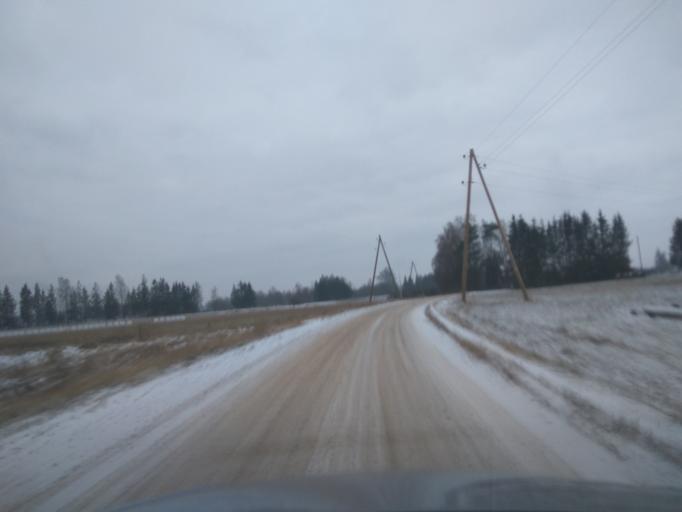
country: LV
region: Aizpute
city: Aizpute
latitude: 56.7349
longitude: 21.6689
